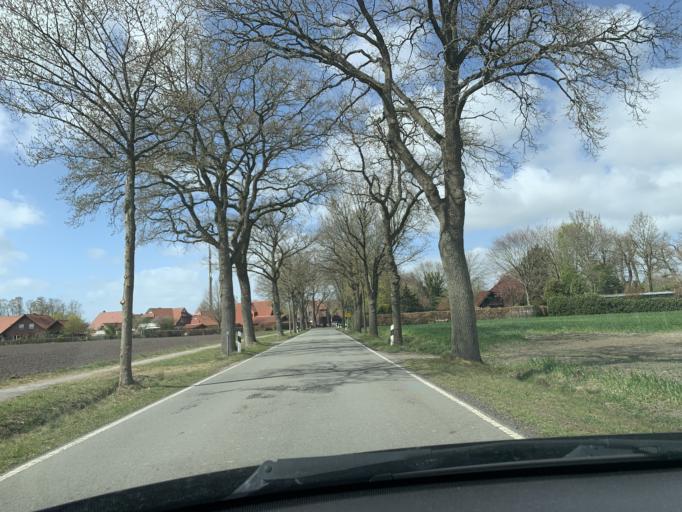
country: DE
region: Lower Saxony
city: Westerstede
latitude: 53.3127
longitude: 7.9238
